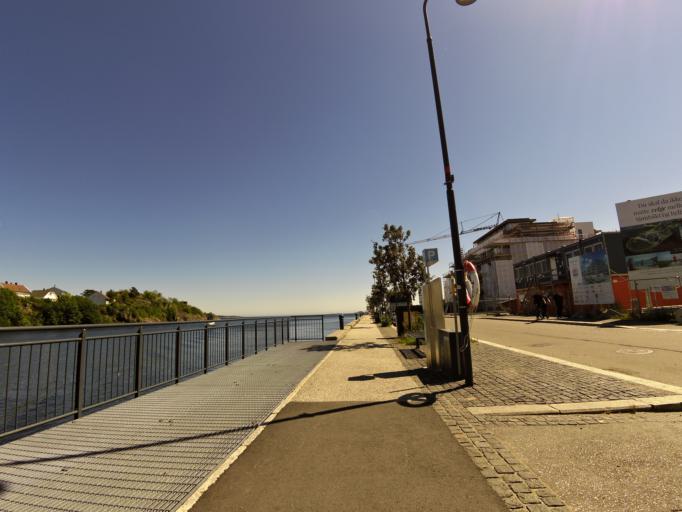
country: NO
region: Vest-Agder
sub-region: Kristiansand
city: Kristiansand
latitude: 58.1455
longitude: 8.0118
